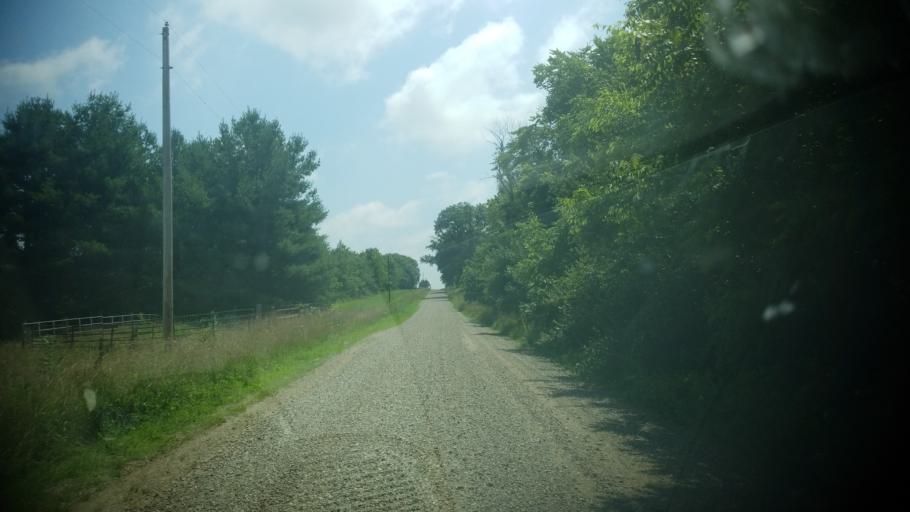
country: US
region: Illinois
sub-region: Wayne County
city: Fairfield
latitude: 38.5300
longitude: -88.3937
